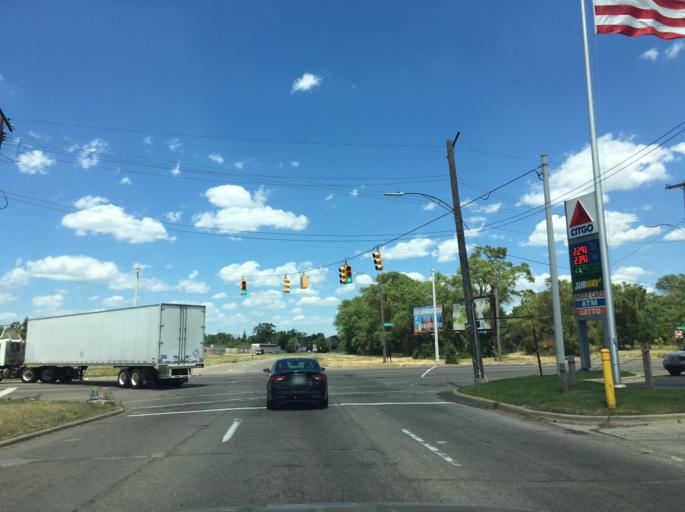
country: US
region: Michigan
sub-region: Wayne County
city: Hamtramck
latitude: 42.4223
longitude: -83.0426
